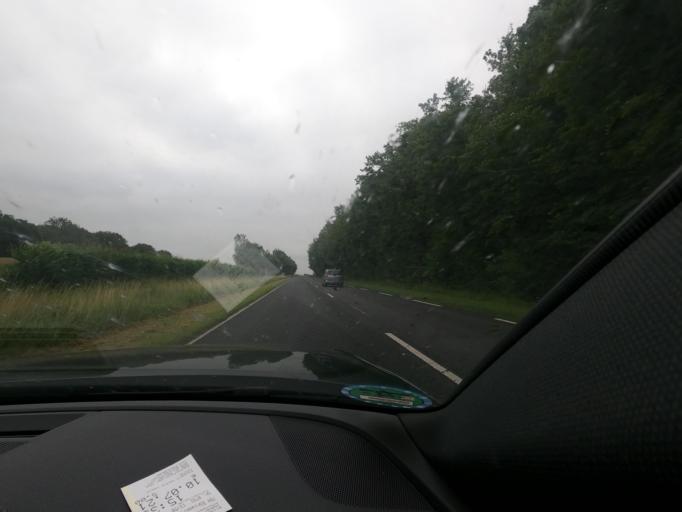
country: FR
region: Picardie
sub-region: Departement de la Somme
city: Moreuil
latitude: 49.7969
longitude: 2.5481
